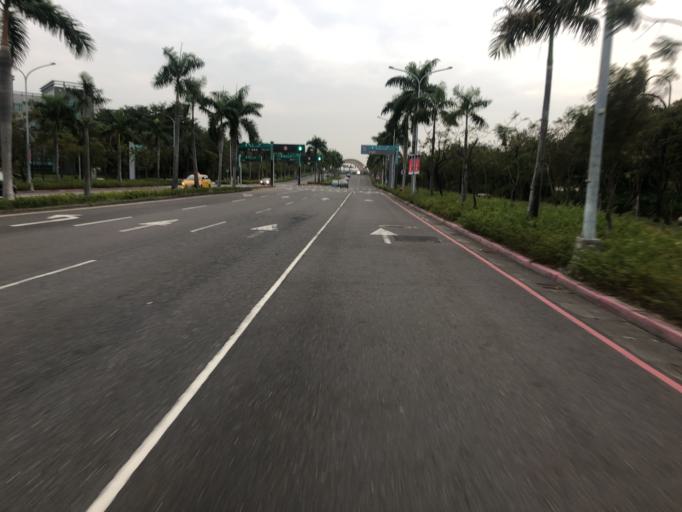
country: TW
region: Taiwan
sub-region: Tainan
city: Tainan
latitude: 23.0944
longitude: 120.2817
